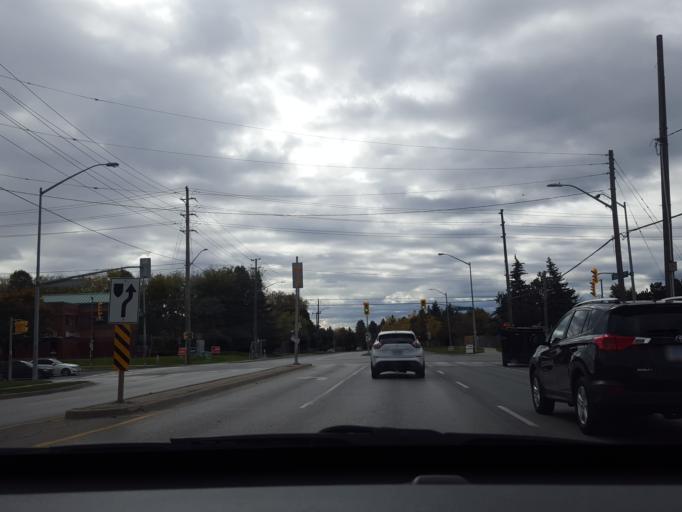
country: CA
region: Ontario
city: Markham
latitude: 43.8801
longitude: -79.3145
